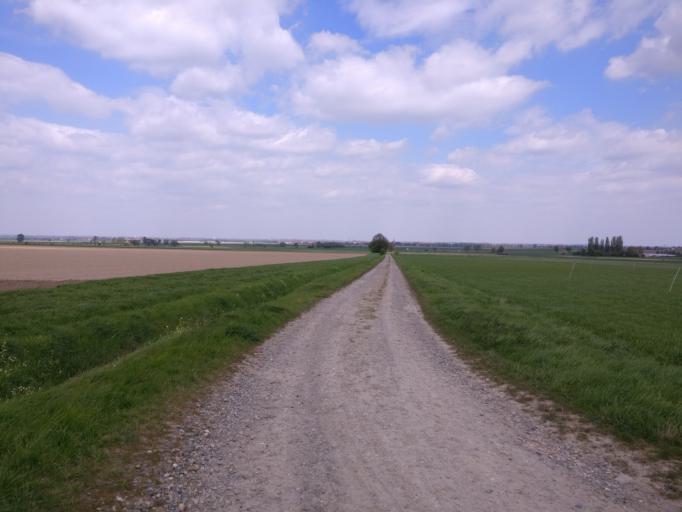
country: DE
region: Lower Saxony
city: Schellerten
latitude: 52.1352
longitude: 10.0566
